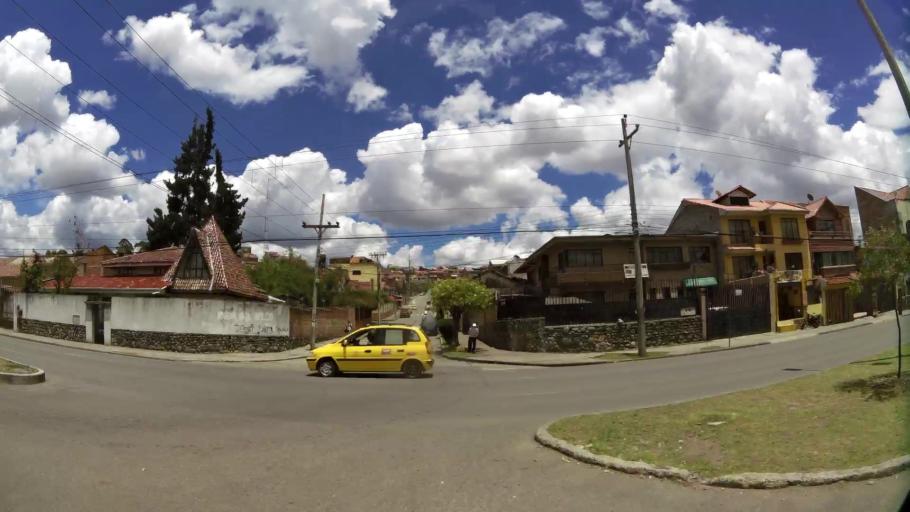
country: EC
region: Azuay
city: Cuenca
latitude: -2.8845
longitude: -79.0033
